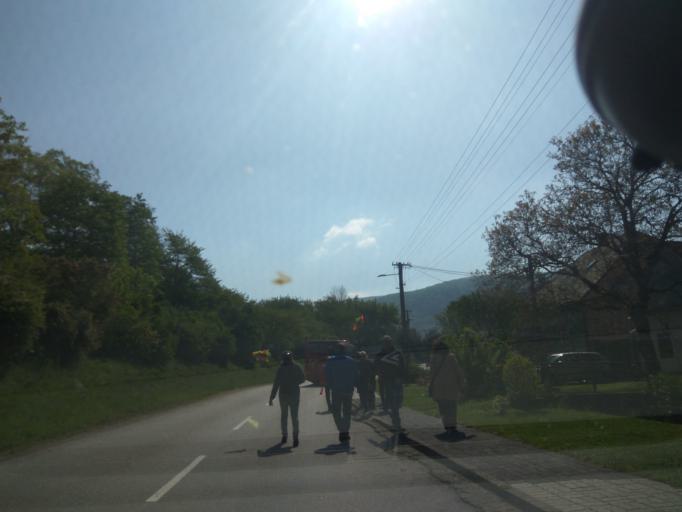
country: SK
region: Bratislavsky
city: Modra
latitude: 48.4820
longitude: 17.2632
